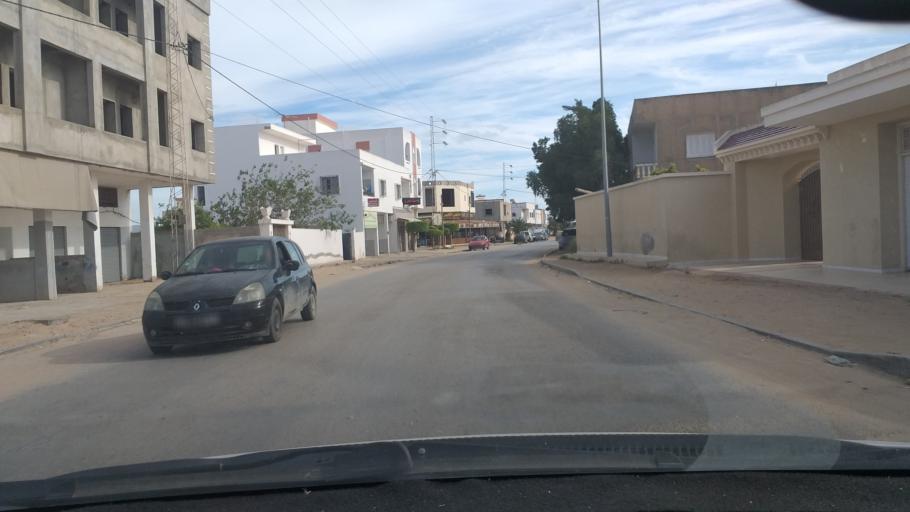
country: TN
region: Safaqis
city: Al Qarmadah
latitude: 34.7933
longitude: 10.8036
